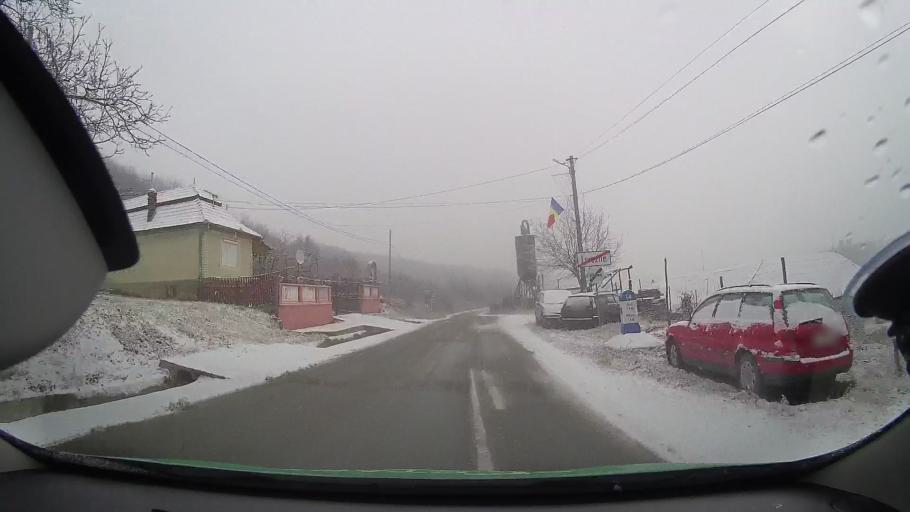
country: RO
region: Alba
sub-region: Comuna Livezile
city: Livezile
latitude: 46.3464
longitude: 23.6503
